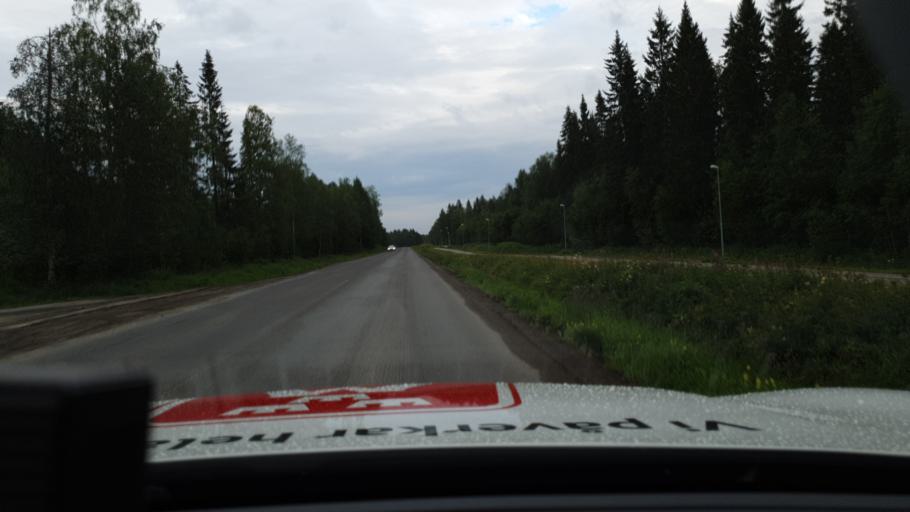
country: SE
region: Norrbotten
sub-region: Bodens Kommun
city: Boden
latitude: 65.8297
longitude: 21.6331
